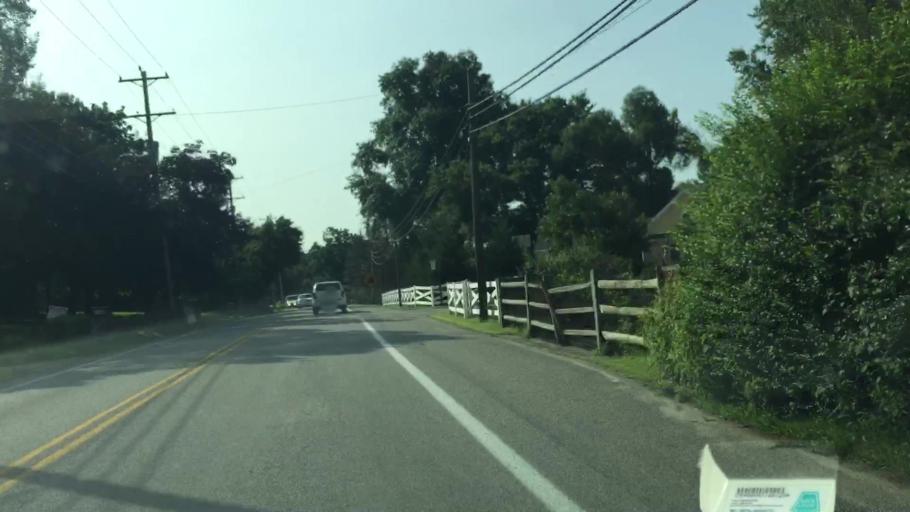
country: US
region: Pennsylvania
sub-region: Allegheny County
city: Verona
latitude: 40.5119
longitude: -79.8571
